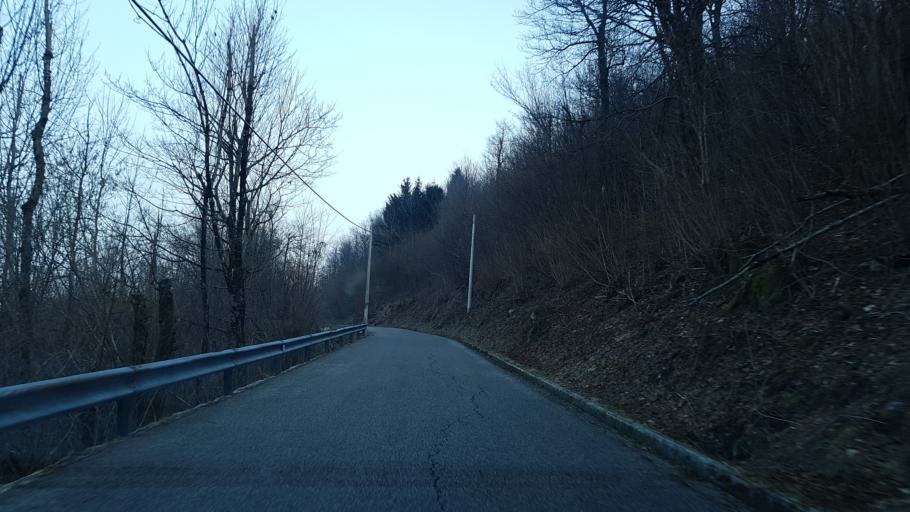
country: IT
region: Friuli Venezia Giulia
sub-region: Provincia di Udine
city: Taipana
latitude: 46.2535
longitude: 13.3688
